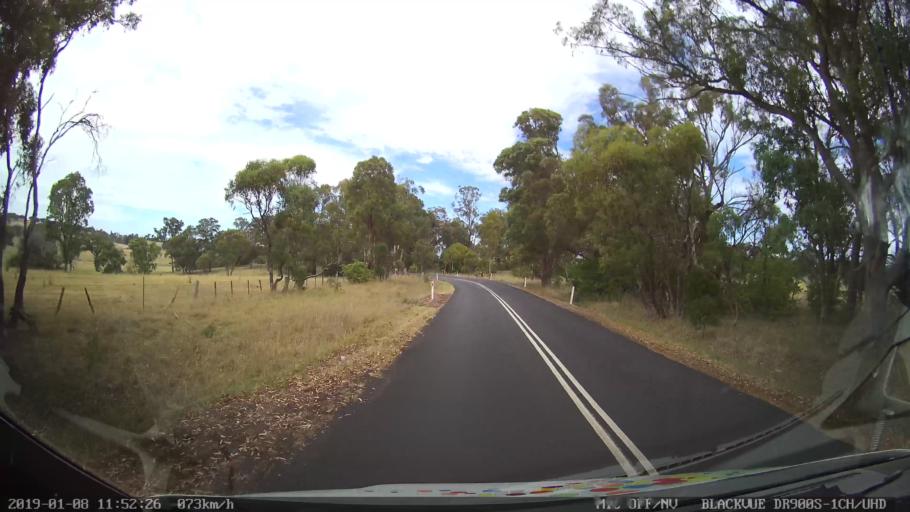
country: AU
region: New South Wales
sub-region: Armidale Dumaresq
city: Armidale
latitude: -30.4038
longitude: 151.5601
